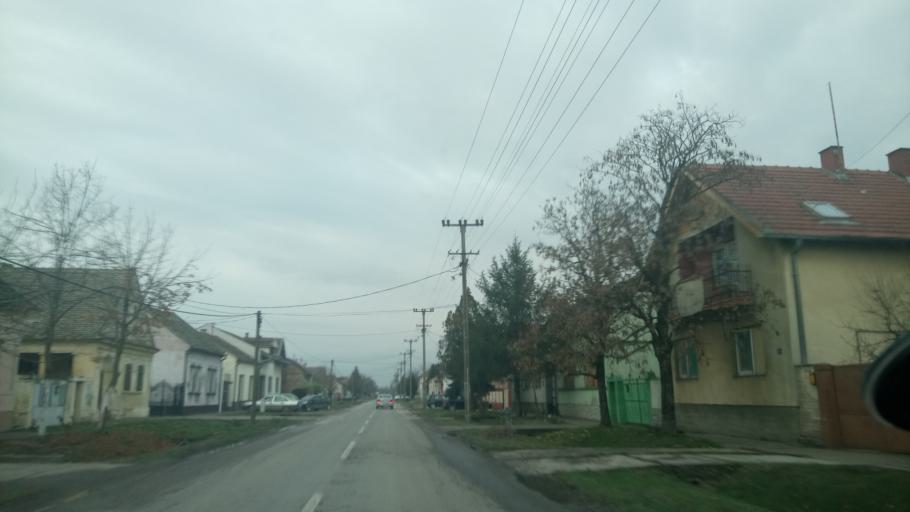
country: RS
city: Vojka
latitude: 44.9393
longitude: 20.1524
